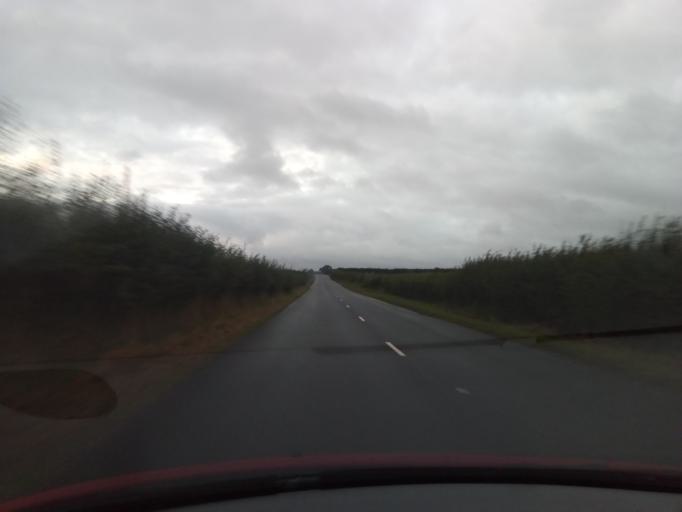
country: GB
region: England
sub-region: Darlington
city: Denton
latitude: 54.5585
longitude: -1.6757
